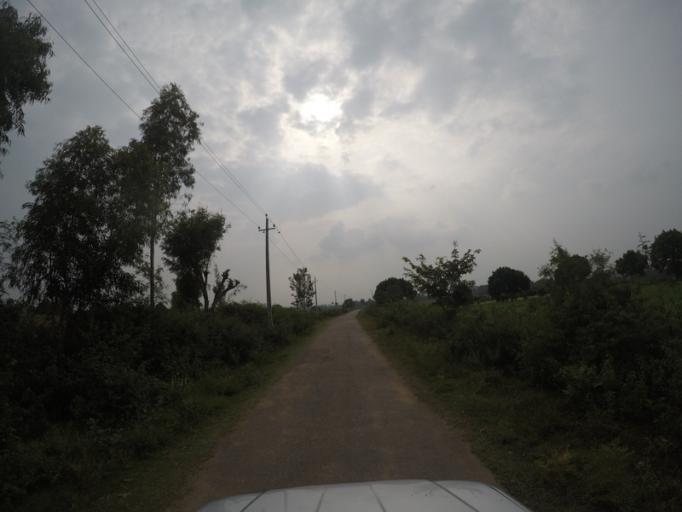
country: IN
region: Karnataka
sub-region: Hassan
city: Belur
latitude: 13.1746
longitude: 75.9193
